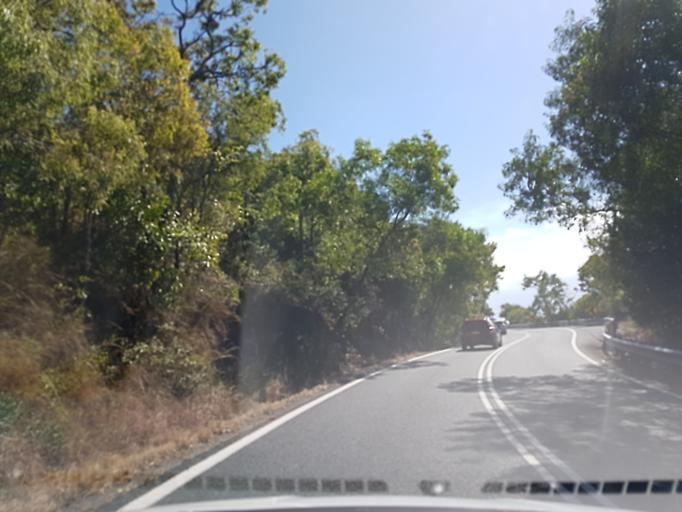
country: AU
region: Queensland
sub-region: Cairns
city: Port Douglas
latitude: -16.6257
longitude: 145.5470
